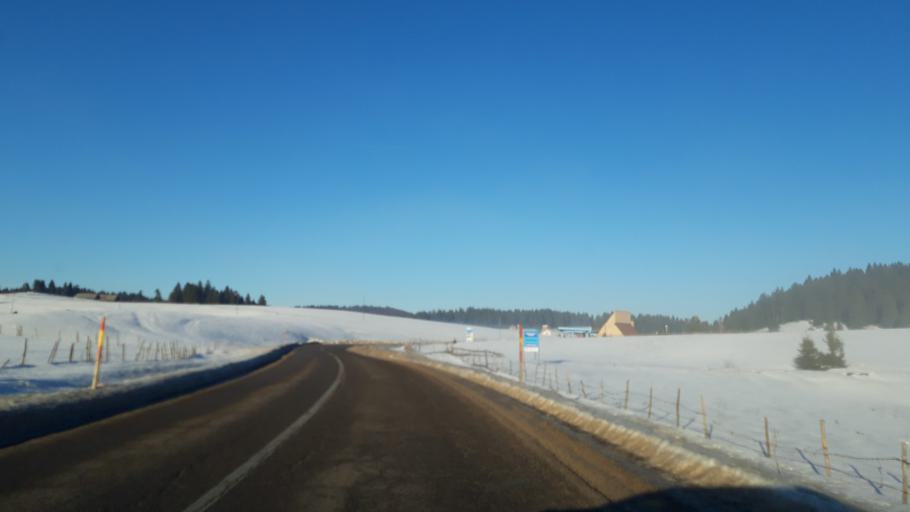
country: BA
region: Republika Srpska
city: Han Pijesak
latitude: 44.1000
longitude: 18.9660
